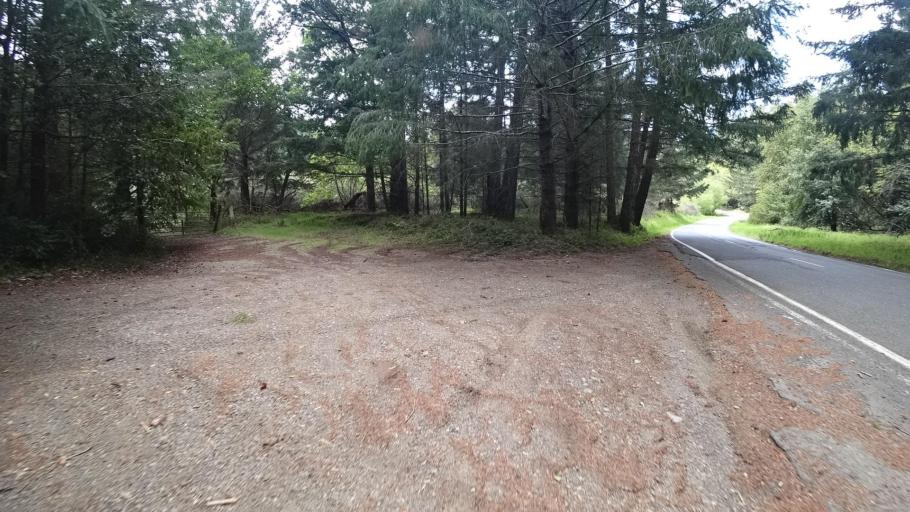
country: US
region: California
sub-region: Humboldt County
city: Redway
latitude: 40.0382
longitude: -124.0237
